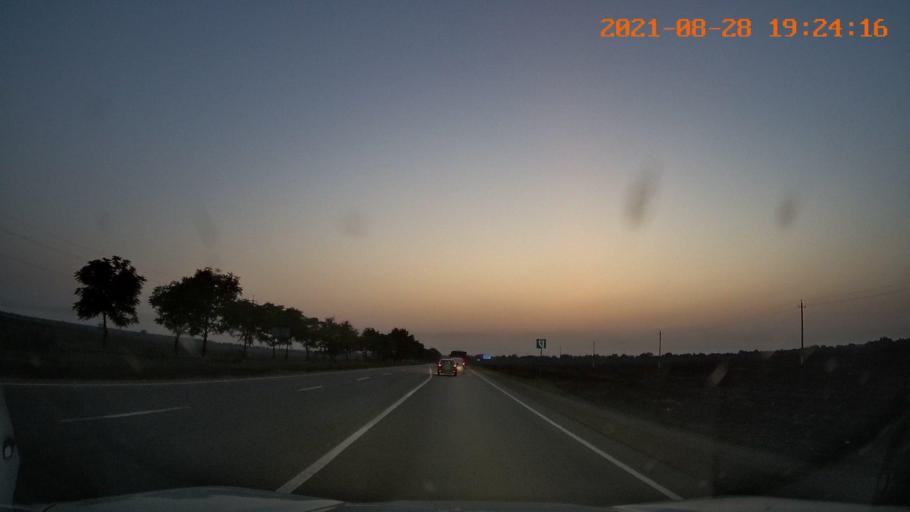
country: RU
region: Adygeya
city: Ponezhukay
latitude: 44.8728
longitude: 39.4363
